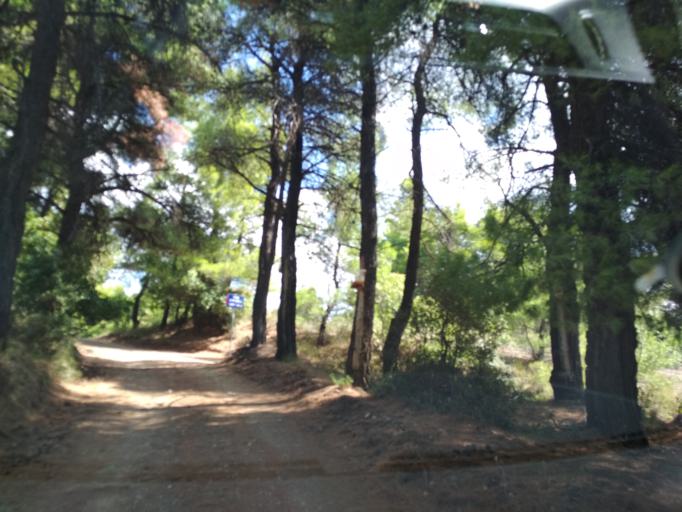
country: GR
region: Central Greece
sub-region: Nomos Evvoias
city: Roviai
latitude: 38.8348
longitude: 23.2775
